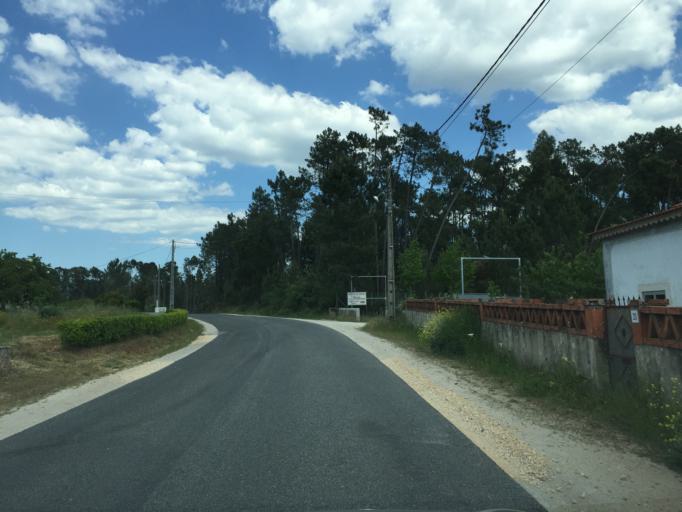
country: PT
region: Santarem
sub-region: Ourem
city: Ourem
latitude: 39.6855
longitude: -8.5591
